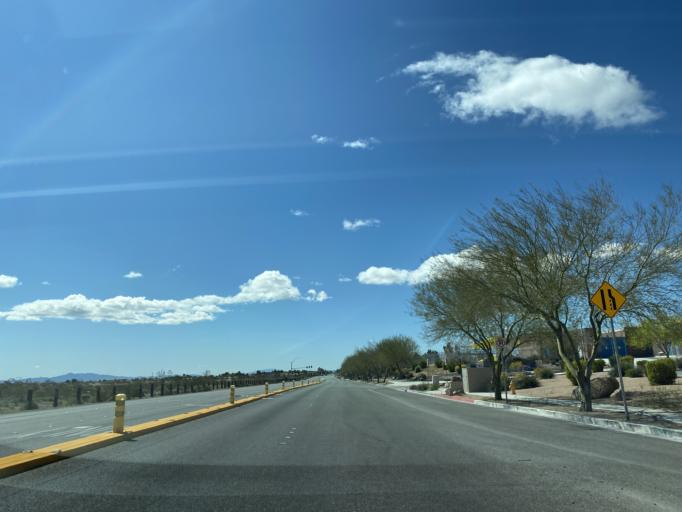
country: US
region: Nevada
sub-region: Clark County
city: North Las Vegas
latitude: 36.3249
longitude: -115.2786
